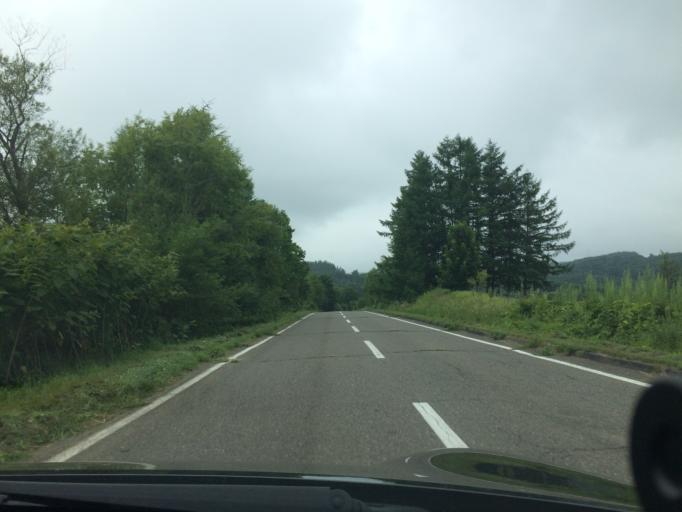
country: JP
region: Hokkaido
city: Otofuke
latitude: 43.0001
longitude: 143.0841
